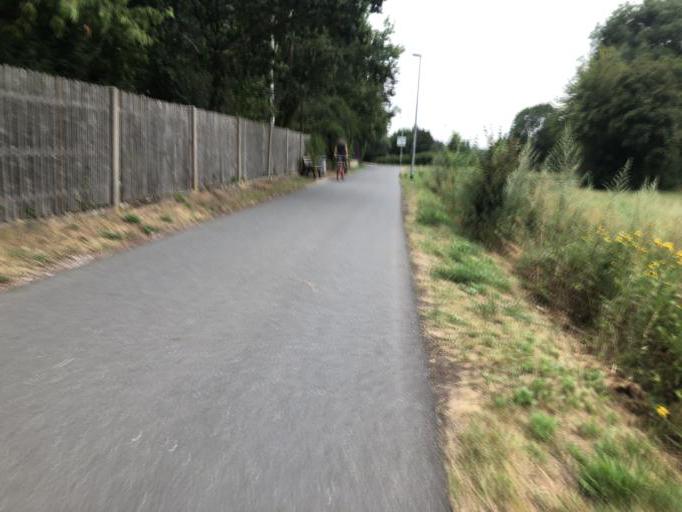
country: DE
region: Bavaria
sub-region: Regierungsbezirk Mittelfranken
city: Furth
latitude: 49.5062
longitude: 10.9755
